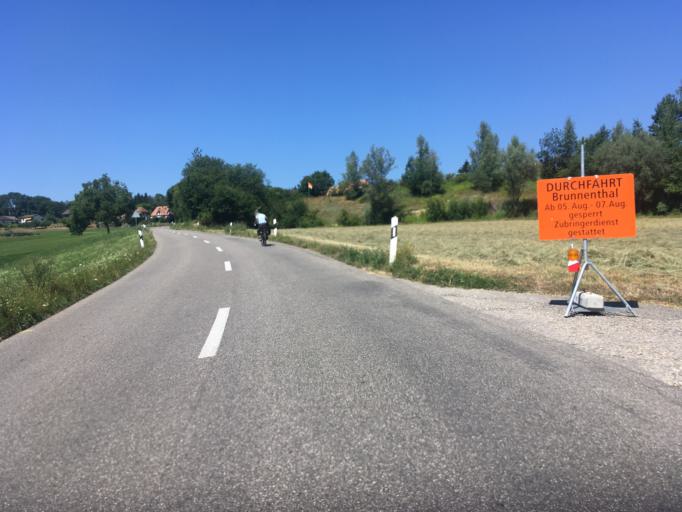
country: CH
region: Solothurn
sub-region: Bezirk Bucheggberg
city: Messen
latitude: 47.0852
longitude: 7.4722
